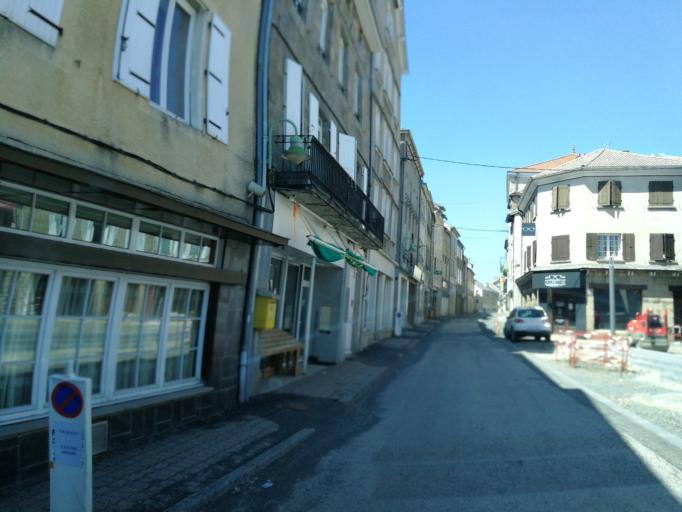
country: FR
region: Rhone-Alpes
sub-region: Departement de l'Ardeche
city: Saint-Agreve
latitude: 45.0091
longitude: 4.3986
